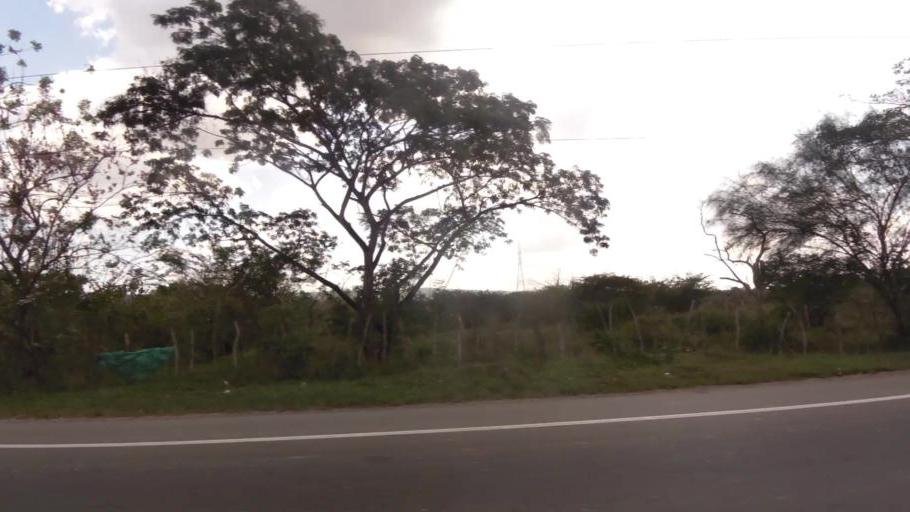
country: CO
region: Bolivar
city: Turbaco
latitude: 10.3643
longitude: -75.4596
